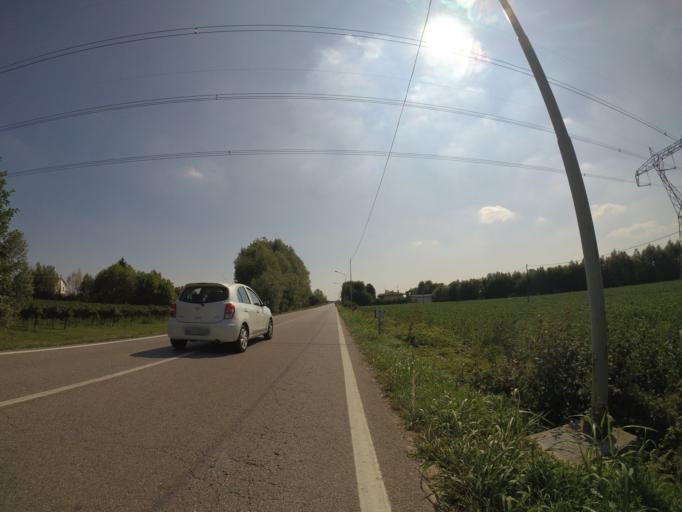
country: IT
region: Friuli Venezia Giulia
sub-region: Provincia di Udine
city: Pocenia
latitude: 45.8258
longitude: 13.1006
